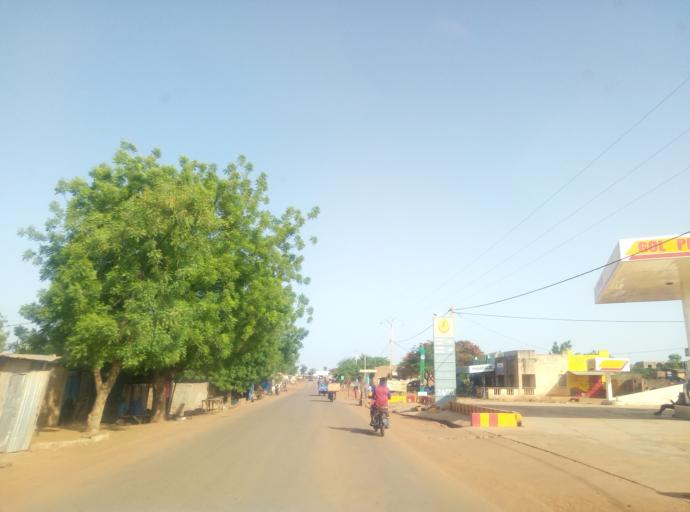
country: ML
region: Bamako
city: Bamako
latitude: 12.6119
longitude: -7.7759
